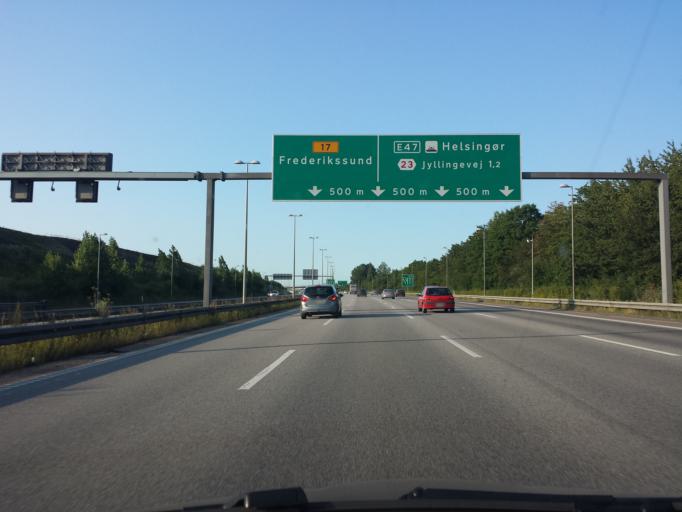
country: DK
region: Capital Region
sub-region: Glostrup Kommune
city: Glostrup
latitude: 55.6785
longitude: 12.4264
